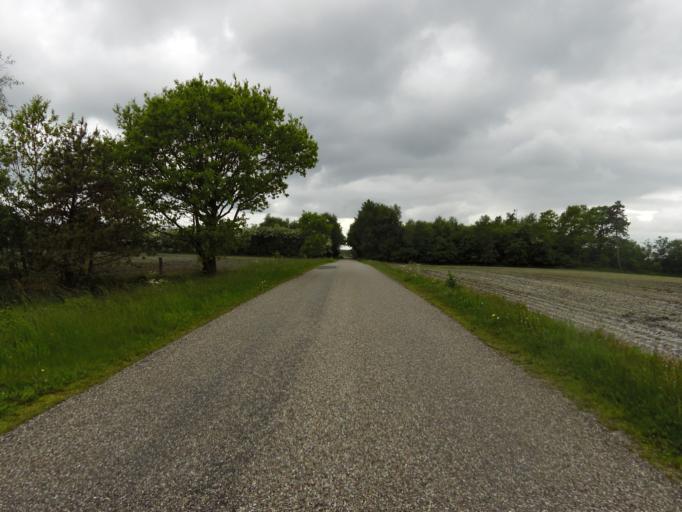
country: DK
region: South Denmark
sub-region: Tonder Kommune
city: Toftlund
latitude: 55.2102
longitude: 9.0227
